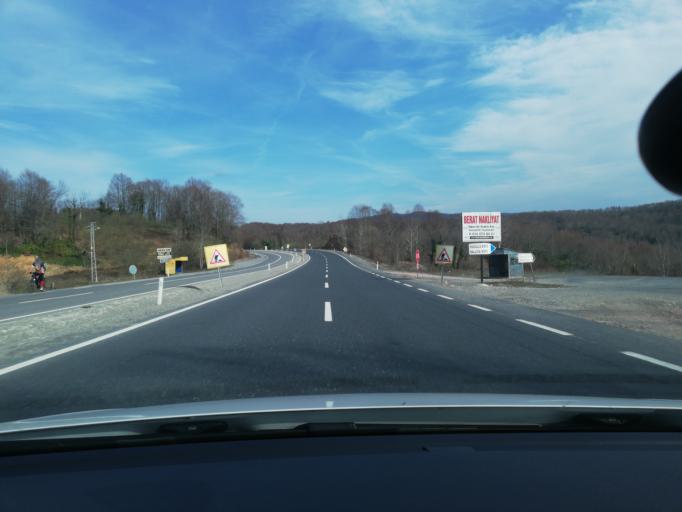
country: TR
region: Zonguldak
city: Kozlu
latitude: 41.3325
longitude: 31.6175
